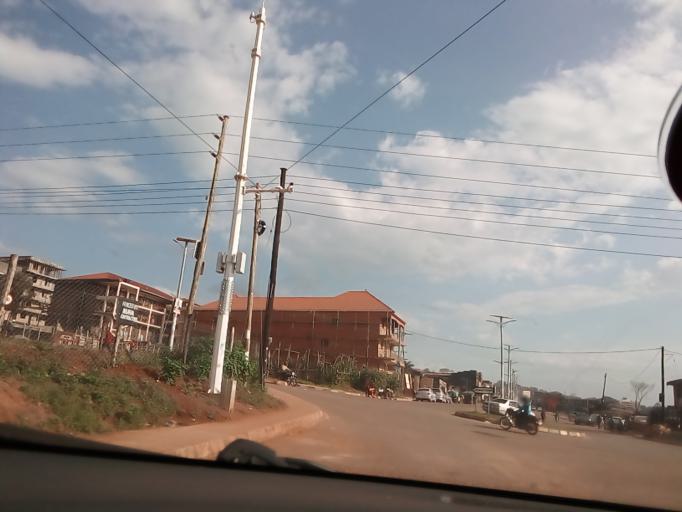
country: UG
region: Central Region
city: Masaka
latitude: -0.3475
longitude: 31.7414
